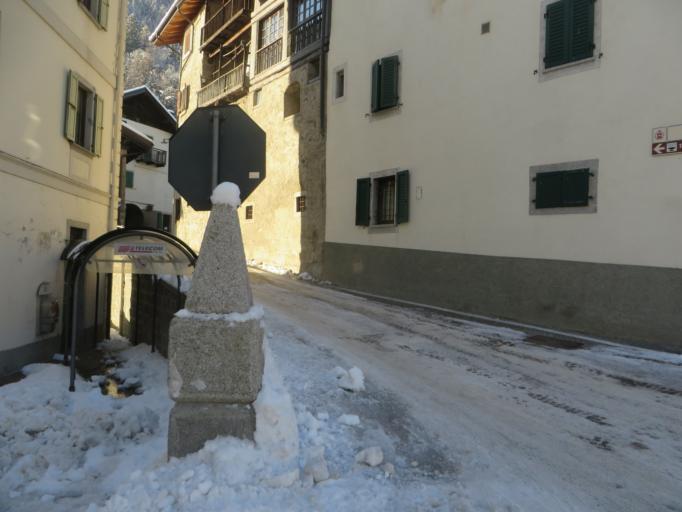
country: IT
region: Trentino-Alto Adige
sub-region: Provincia di Trento
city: Caderzone Terme
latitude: 46.1294
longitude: 10.7567
